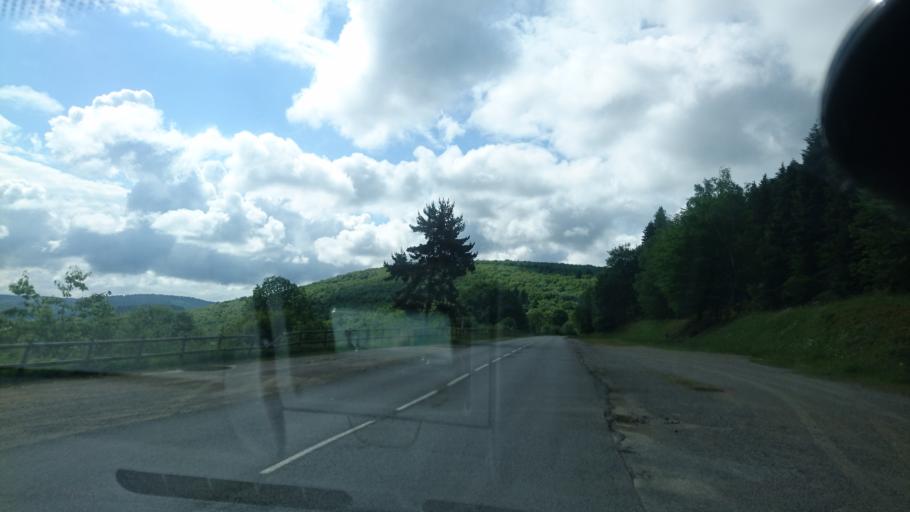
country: FR
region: Limousin
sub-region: Departement de la Haute-Vienne
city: Peyrat-le-Chateau
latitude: 45.7994
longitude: 1.8404
